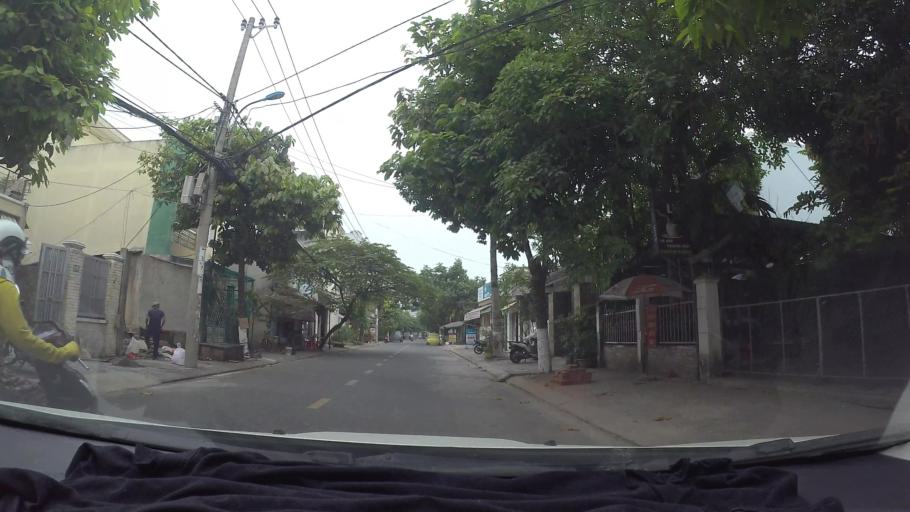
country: VN
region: Da Nang
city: Cam Le
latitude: 16.0232
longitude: 108.2110
